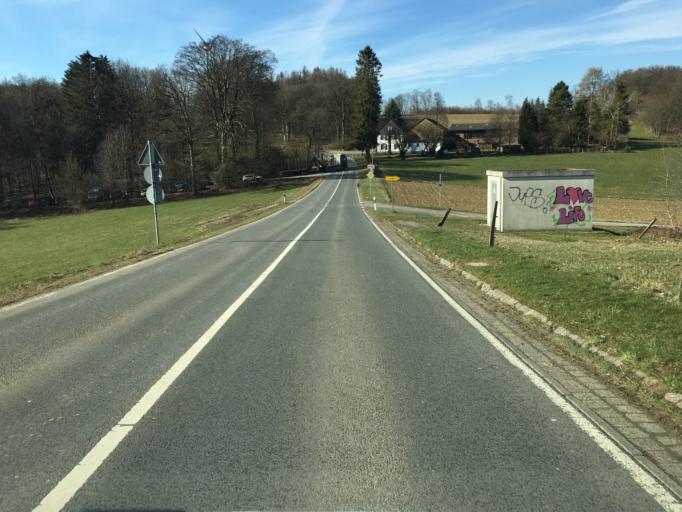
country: DE
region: North Rhine-Westphalia
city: Huckeswagen
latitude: 51.1304
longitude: 7.3278
